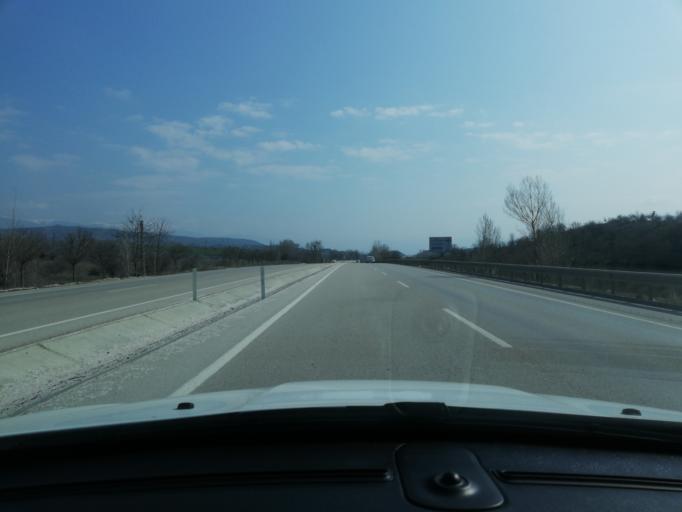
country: TR
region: Cankiri
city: Beloren
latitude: 40.8717
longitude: 33.4961
